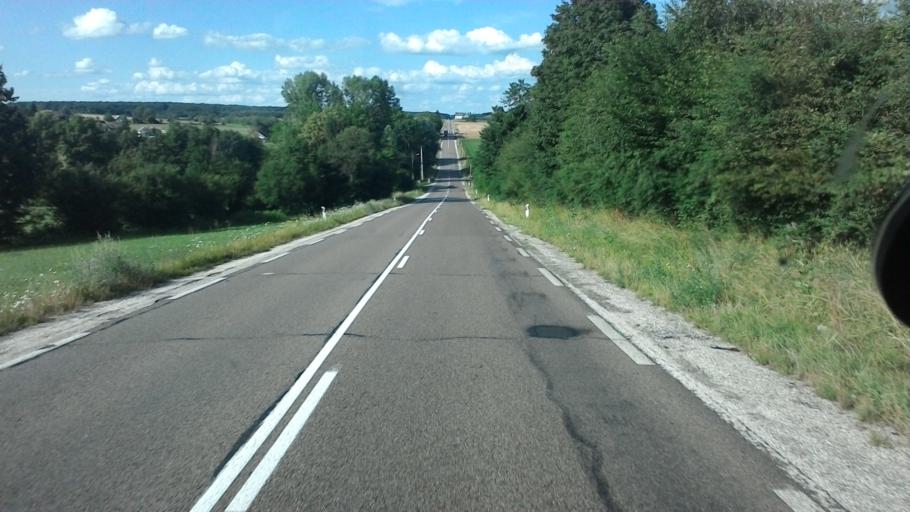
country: FR
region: Franche-Comte
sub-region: Departement de la Haute-Saone
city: Luxeuil-les-Bains
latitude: 47.7172
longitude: 6.3020
